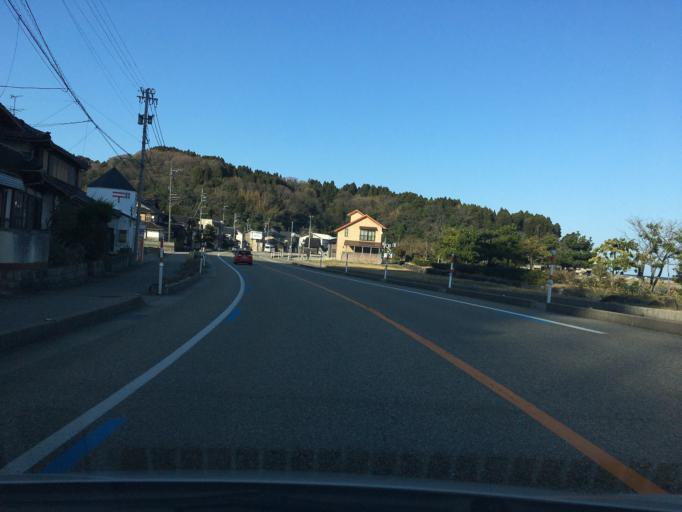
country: JP
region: Toyama
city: Himi
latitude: 36.8879
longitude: 136.9981
